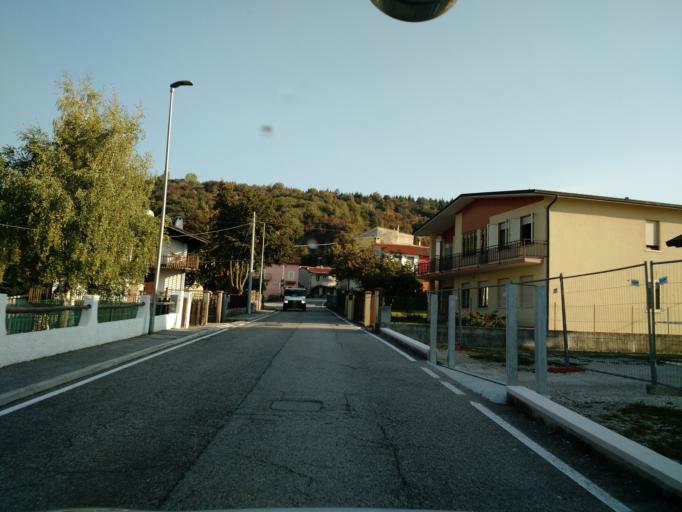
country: IT
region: Veneto
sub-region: Provincia di Vicenza
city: Lusiana
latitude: 45.7823
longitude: 11.5688
